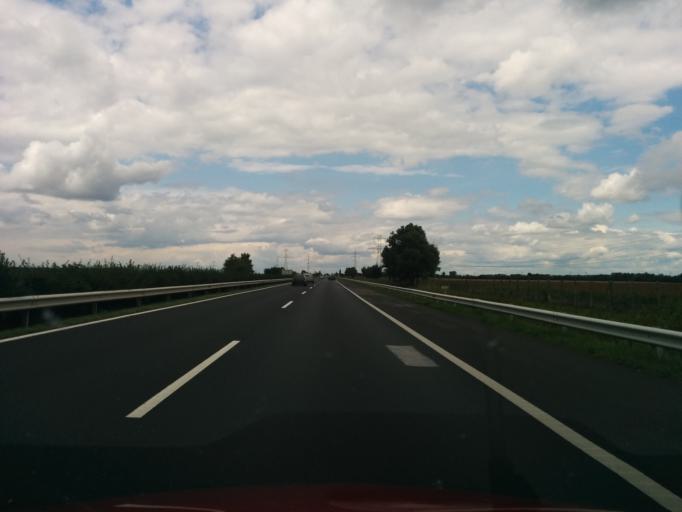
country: HU
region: Gyor-Moson-Sopron
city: Mosonmagyarovar
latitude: 47.8122
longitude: 17.2941
